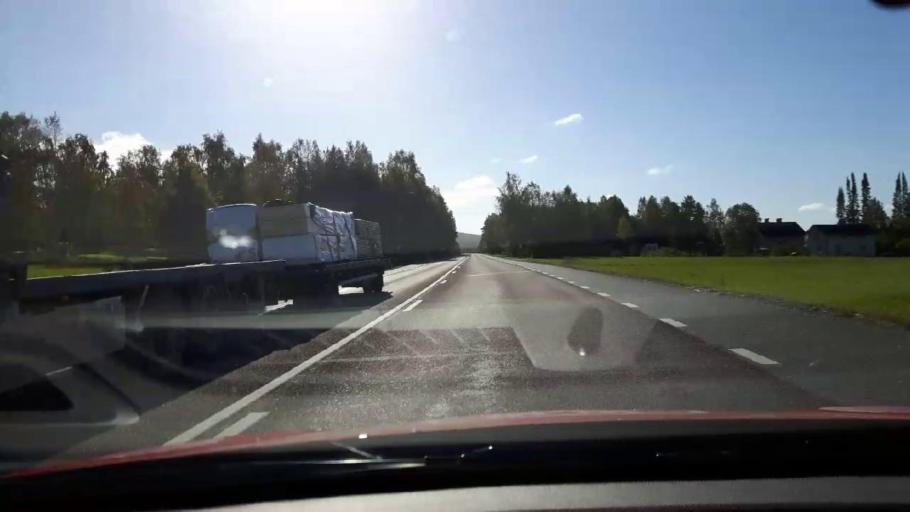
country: SE
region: Jaemtland
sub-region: Braecke Kommun
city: Braecke
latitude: 62.8271
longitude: 15.3189
